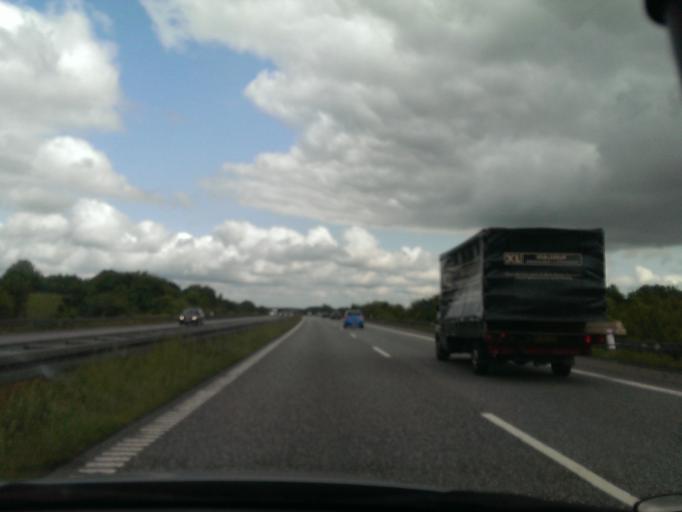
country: DK
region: North Denmark
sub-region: Mariagerfjord Kommune
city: Hobro
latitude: 56.6430
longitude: 9.7376
